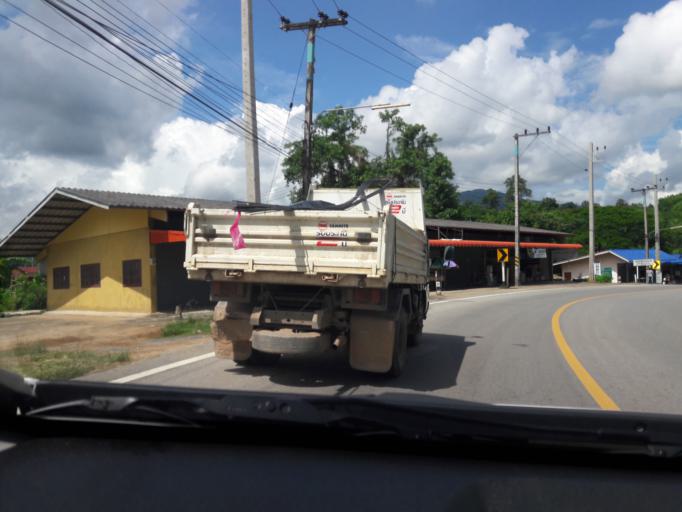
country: TH
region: Chiang Mai
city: Mae Taeng
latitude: 19.1043
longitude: 98.8374
